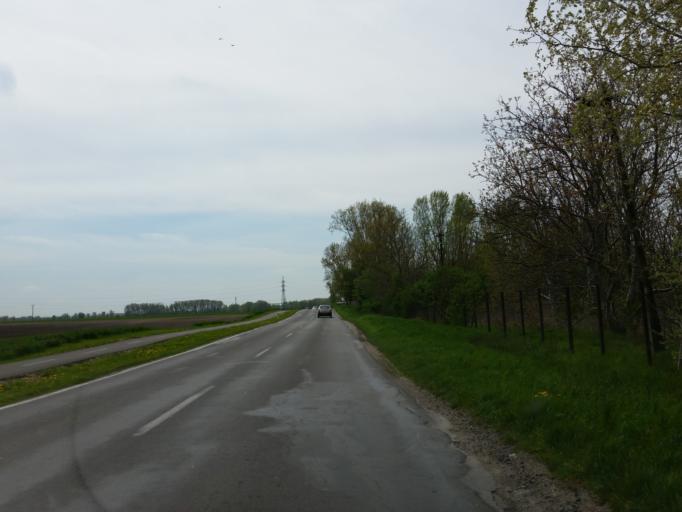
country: SK
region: Trnavsky
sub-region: Okres Dunajska Streda
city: Velky Meder
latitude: 47.8824
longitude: 17.8036
